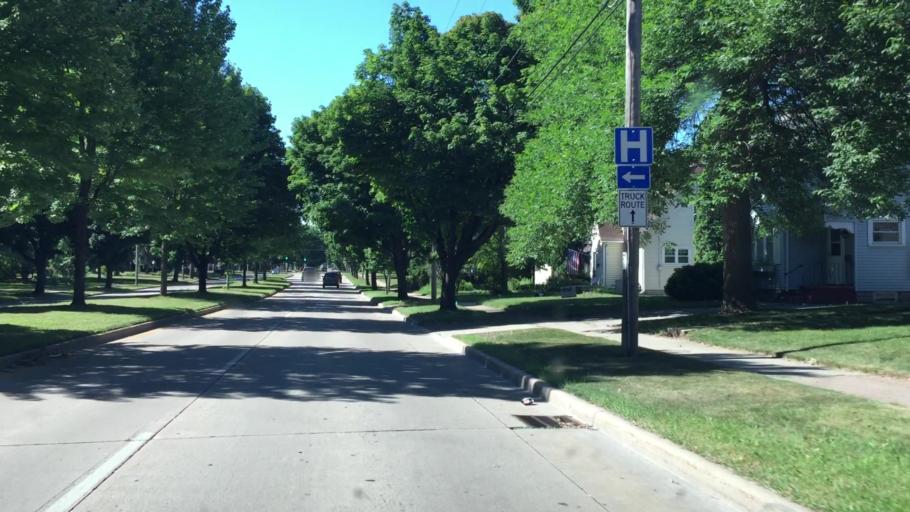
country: US
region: Wisconsin
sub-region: Outagamie County
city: Appleton
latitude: 44.2496
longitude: -88.4158
